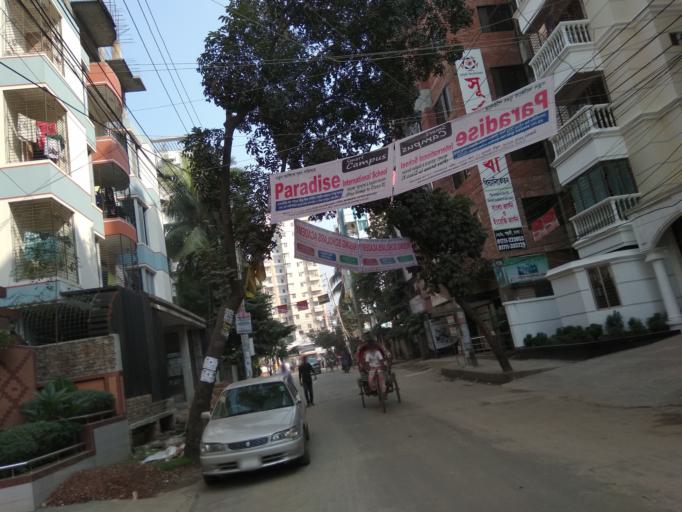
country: BD
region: Dhaka
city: Tungi
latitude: 23.8264
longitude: 90.3629
